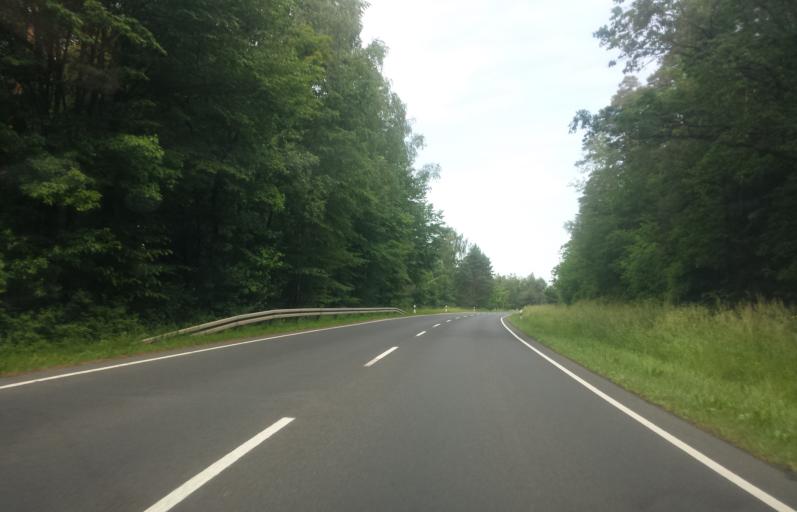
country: DE
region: Bavaria
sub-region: Upper Palatinate
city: Pressath
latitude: 49.7555
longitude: 11.9217
